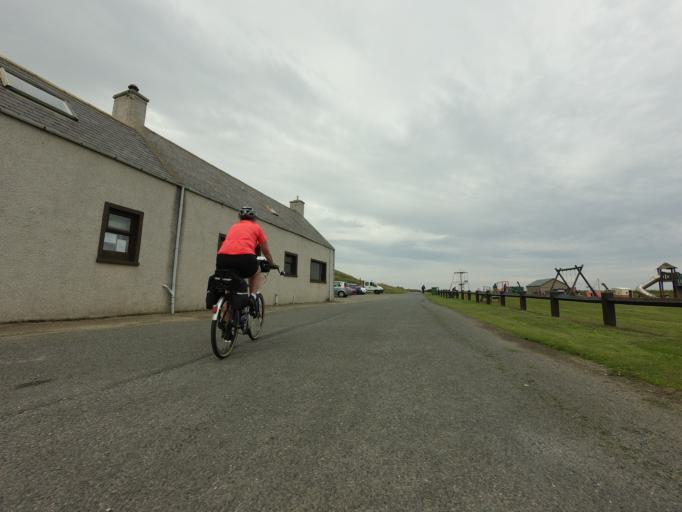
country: GB
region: Scotland
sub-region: Aberdeenshire
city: Whitehills
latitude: 57.6809
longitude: -2.5722
